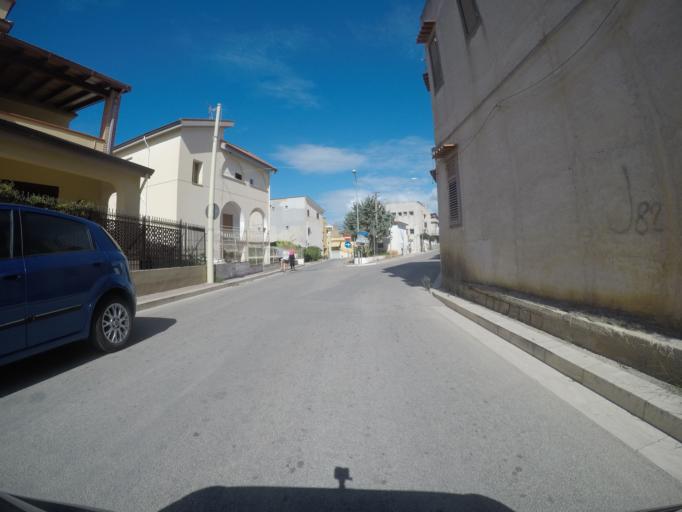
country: IT
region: Sicily
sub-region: Palermo
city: Trappeto
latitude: 38.0663
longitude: 13.0357
